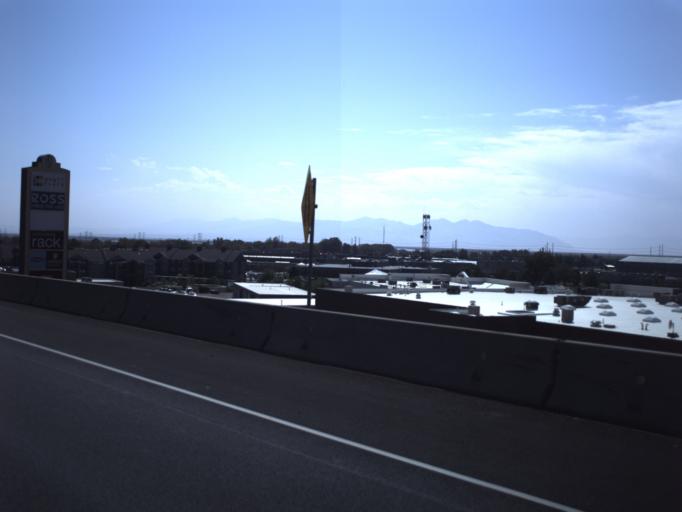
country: US
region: Utah
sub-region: Davis County
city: Farmington
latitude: 40.9850
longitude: -111.9018
